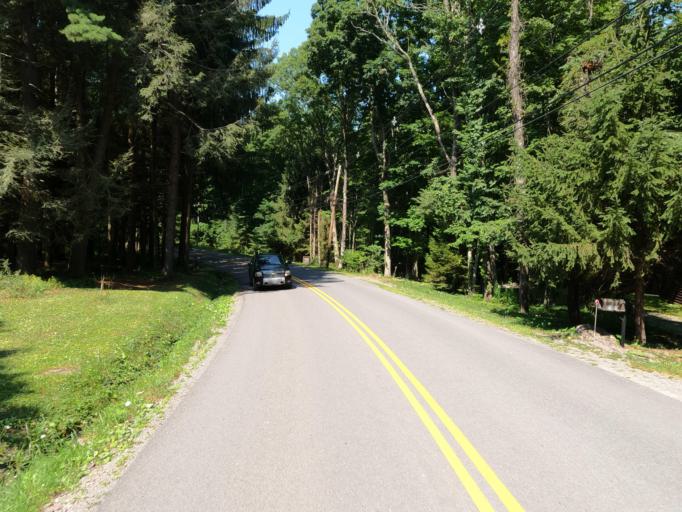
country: US
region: Maryland
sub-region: Garrett County
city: Oakland
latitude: 39.5090
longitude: -79.3851
